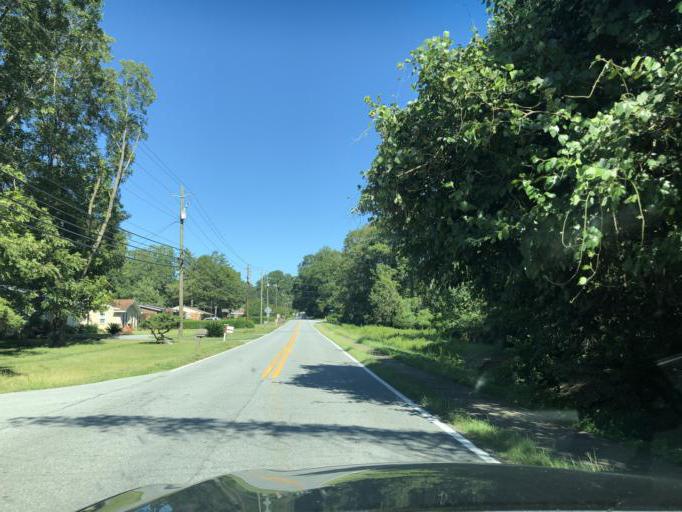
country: US
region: Georgia
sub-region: Muscogee County
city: Columbus
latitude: 32.5068
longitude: -84.9215
